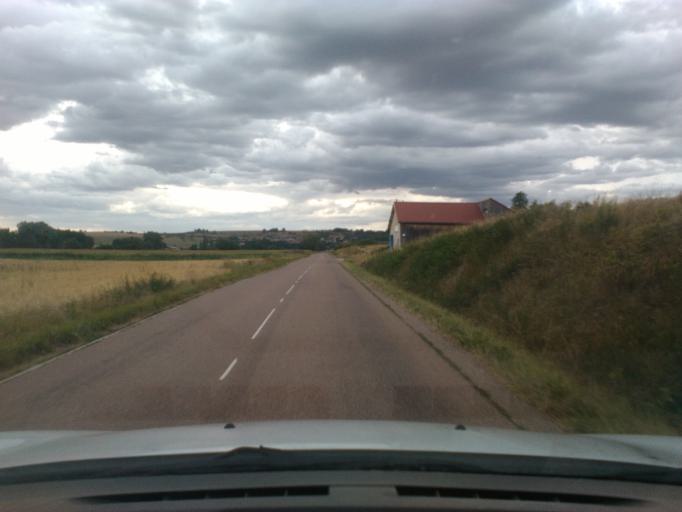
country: FR
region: Lorraine
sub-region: Departement des Vosges
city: Charmes
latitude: 48.3533
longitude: 6.2718
